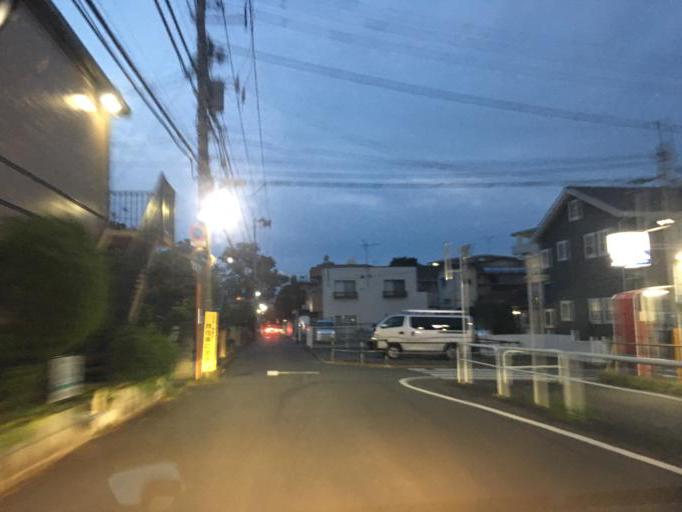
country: JP
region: Tokyo
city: Higashimurayama-shi
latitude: 35.7366
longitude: 139.4532
